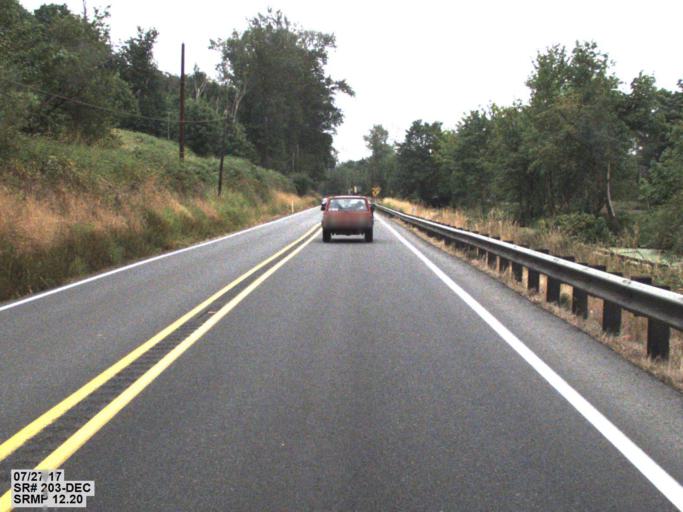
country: US
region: Washington
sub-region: King County
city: Duvall
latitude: 47.7033
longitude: -121.9828
